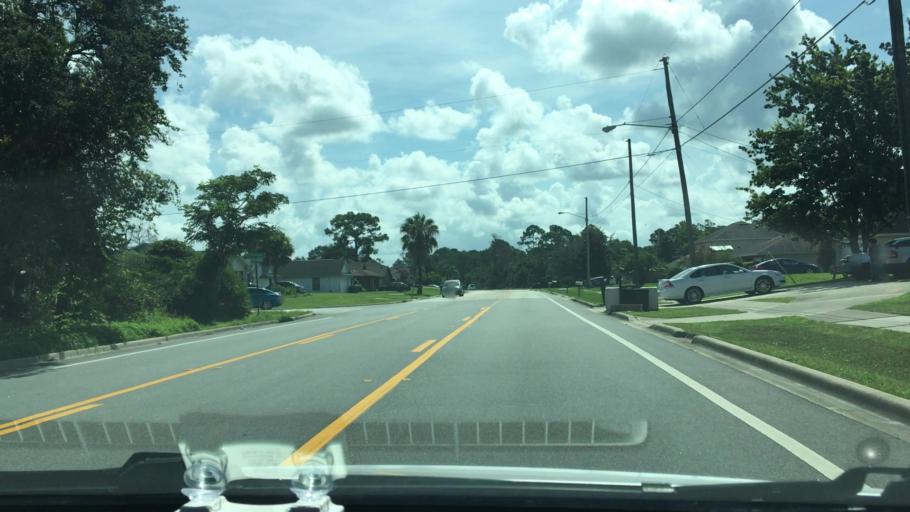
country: US
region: Florida
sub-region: Volusia County
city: Deltona
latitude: 28.8818
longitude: -81.2315
